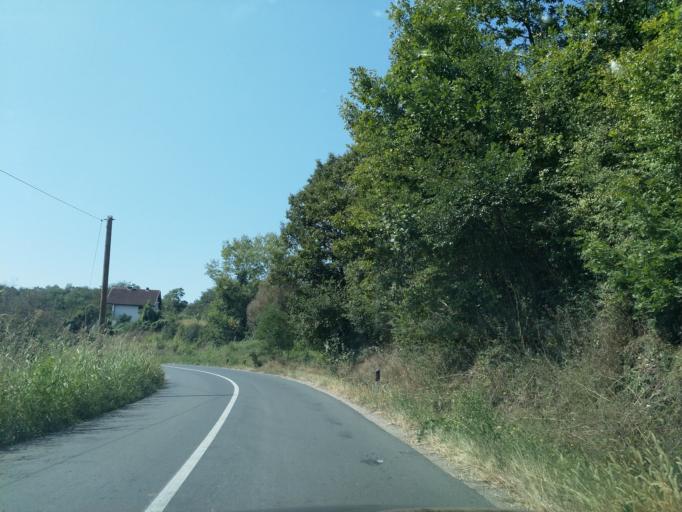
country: RS
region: Central Serbia
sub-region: Rasinski Okrug
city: Krusevac
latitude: 43.6223
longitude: 21.3251
